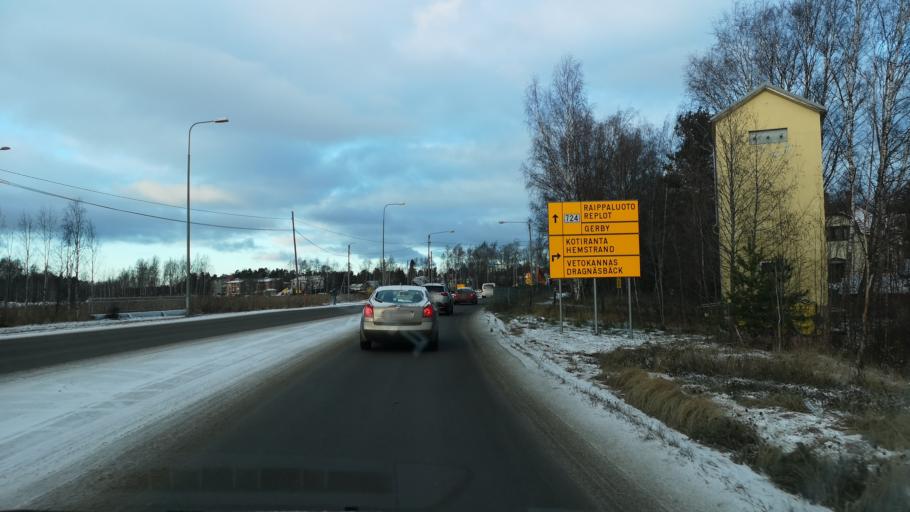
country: FI
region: Ostrobothnia
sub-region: Vaasa
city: Vaasa
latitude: 63.1118
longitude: 21.6190
